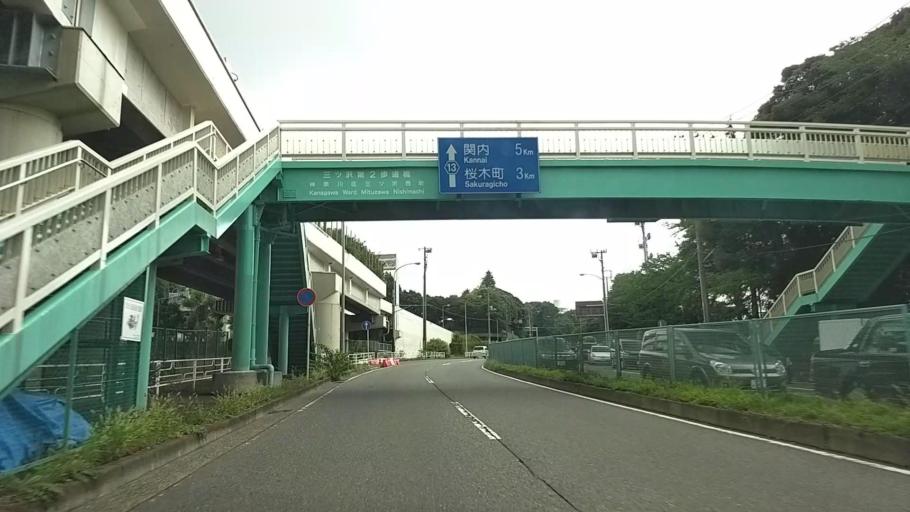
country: JP
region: Kanagawa
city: Yokohama
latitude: 35.4722
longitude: 139.6037
